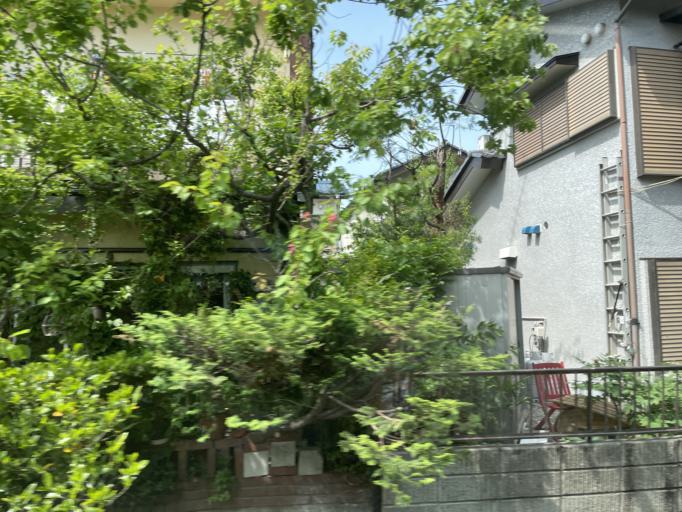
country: JP
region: Saitama
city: Hanno
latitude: 35.8424
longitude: 139.3398
